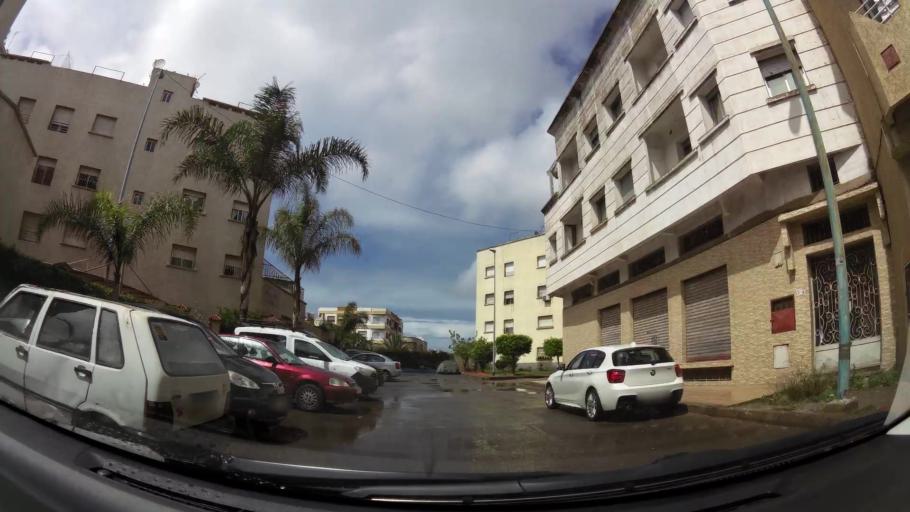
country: MA
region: Grand Casablanca
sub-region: Casablanca
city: Casablanca
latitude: 33.5303
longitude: -7.6515
